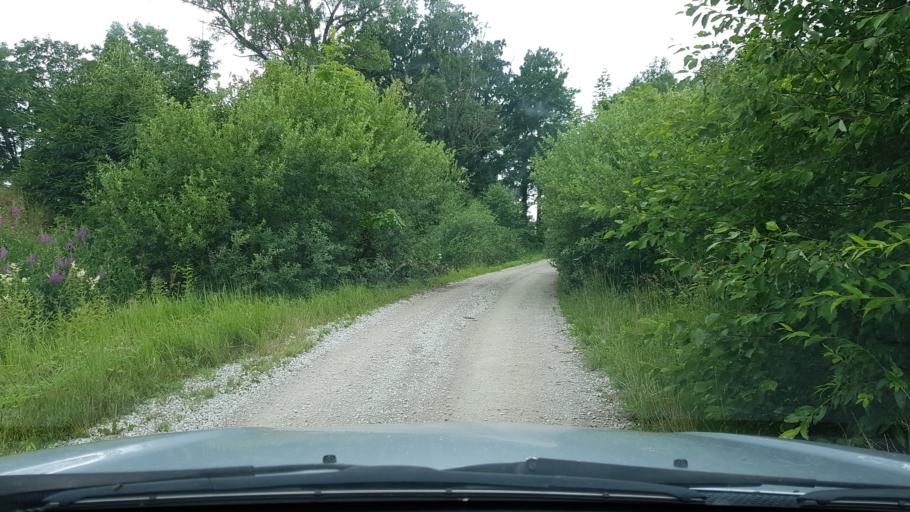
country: EE
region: Ida-Virumaa
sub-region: Narva linn
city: Narva
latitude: 59.3926
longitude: 28.1070
